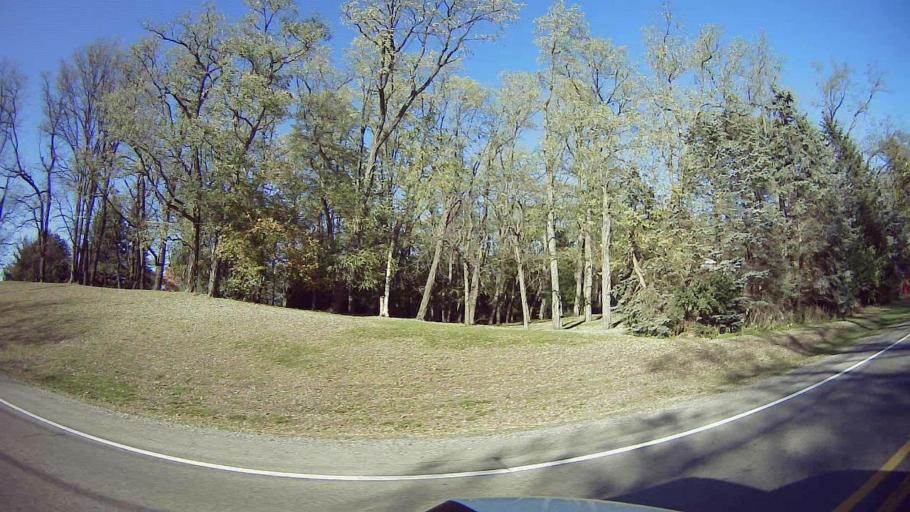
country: US
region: Michigan
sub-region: Oakland County
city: Franklin
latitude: 42.5437
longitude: -83.3327
